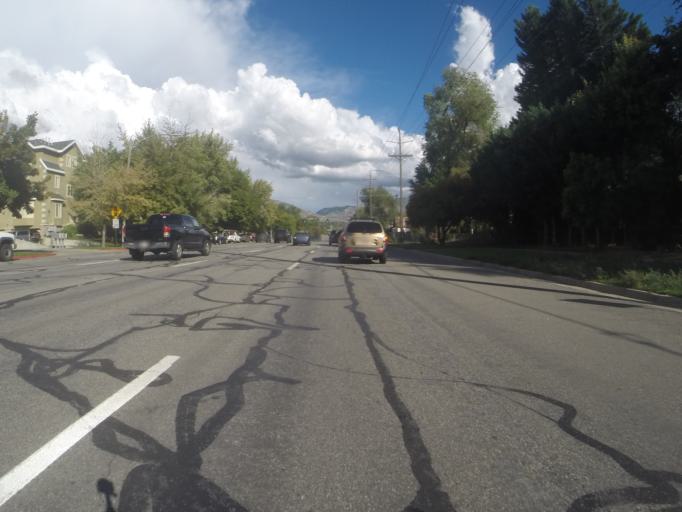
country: US
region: Utah
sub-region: Salt Lake County
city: Salt Lake City
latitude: 40.7563
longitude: -111.8810
